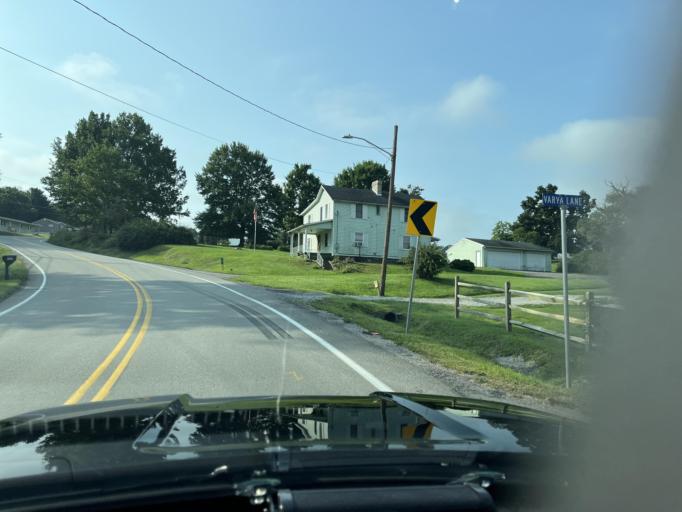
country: US
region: Pennsylvania
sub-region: Fayette County
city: Hopwood
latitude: 39.8613
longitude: -79.7109
